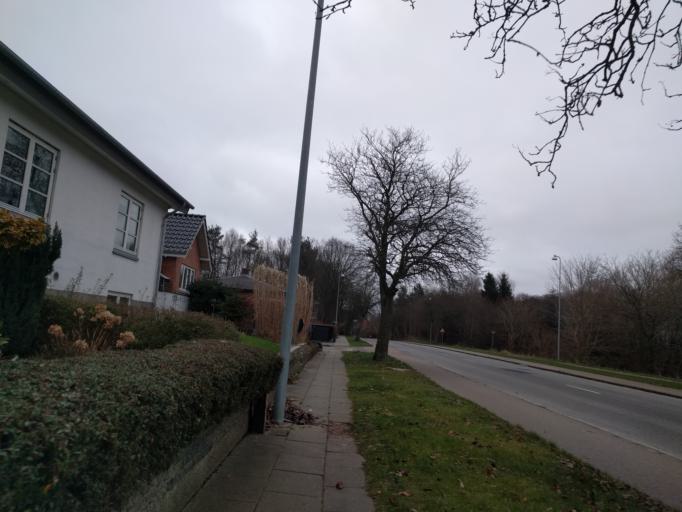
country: DK
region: Central Jutland
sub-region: Viborg Kommune
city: Viborg
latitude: 56.4395
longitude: 9.3996
